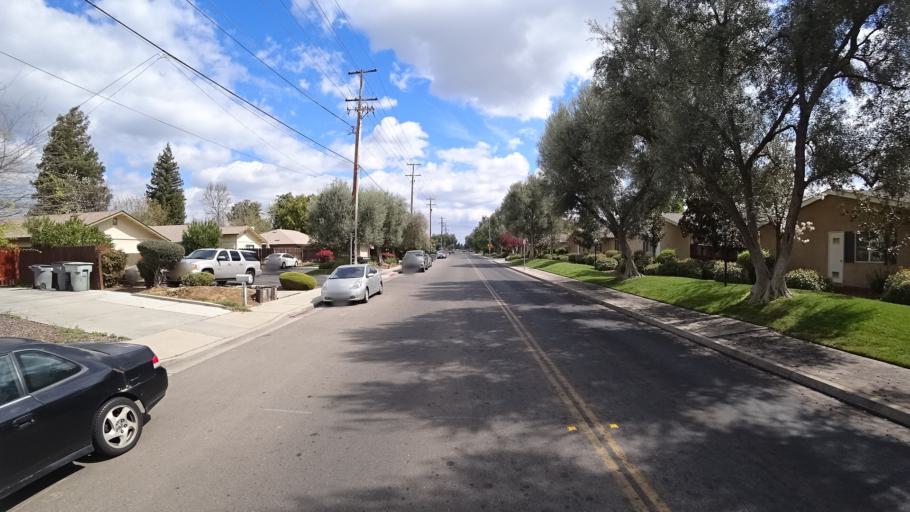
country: US
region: California
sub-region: Fresno County
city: West Park
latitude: 36.8227
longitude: -119.8607
